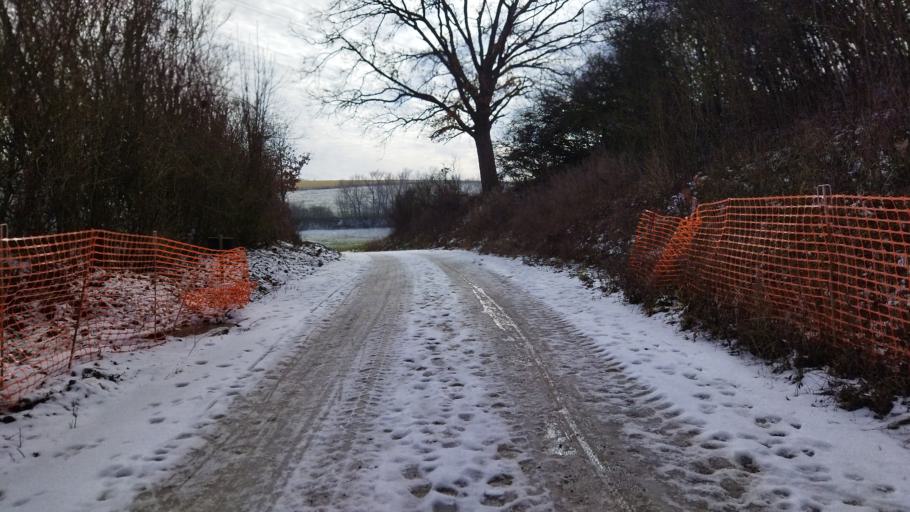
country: DE
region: Baden-Wuerttemberg
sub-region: Regierungsbezirk Stuttgart
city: Bad Wimpfen
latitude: 49.1875
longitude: 9.1551
